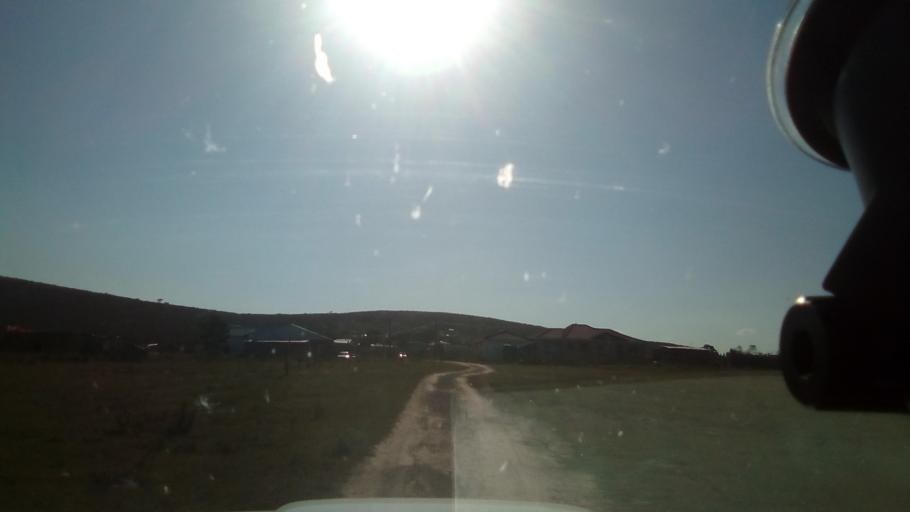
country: ZA
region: Eastern Cape
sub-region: Buffalo City Metropolitan Municipality
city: Bhisho
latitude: -32.8211
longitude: 27.3535
